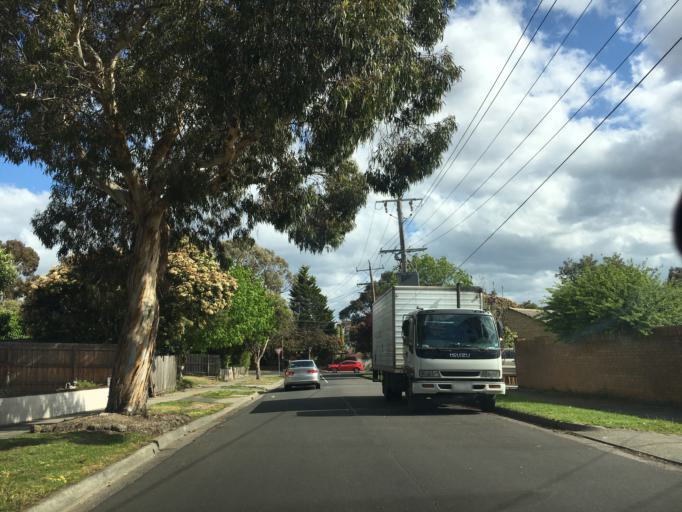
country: AU
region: Victoria
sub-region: Monash
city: Notting Hill
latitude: -37.8886
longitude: 145.1684
